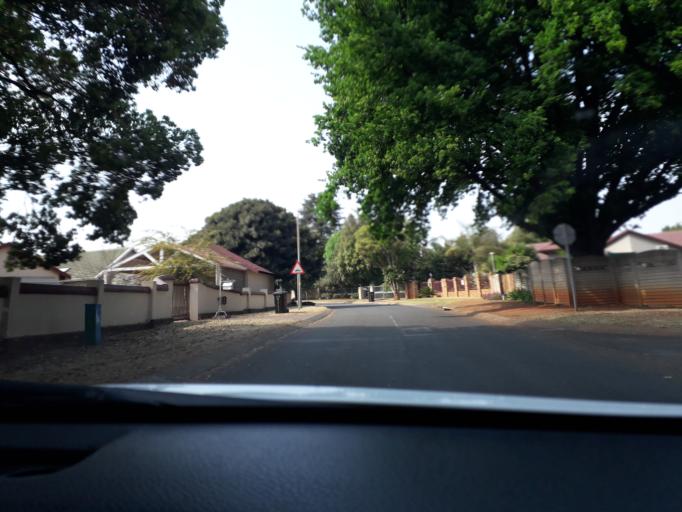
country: ZA
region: Gauteng
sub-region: City of Johannesburg Metropolitan Municipality
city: Modderfontein
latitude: -26.0785
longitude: 28.2393
